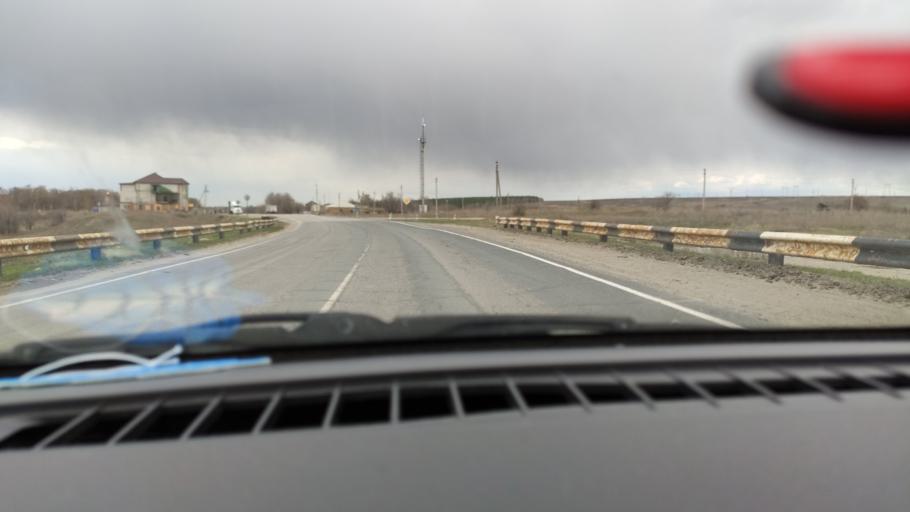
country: RU
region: Saratov
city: Sinodskoye
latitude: 52.0469
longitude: 46.7442
